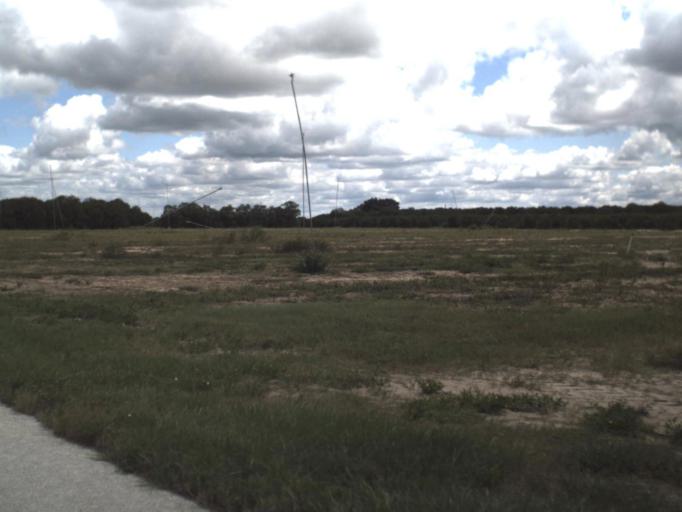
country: US
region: Florida
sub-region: Polk County
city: Fort Meade
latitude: 27.7335
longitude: -81.6992
